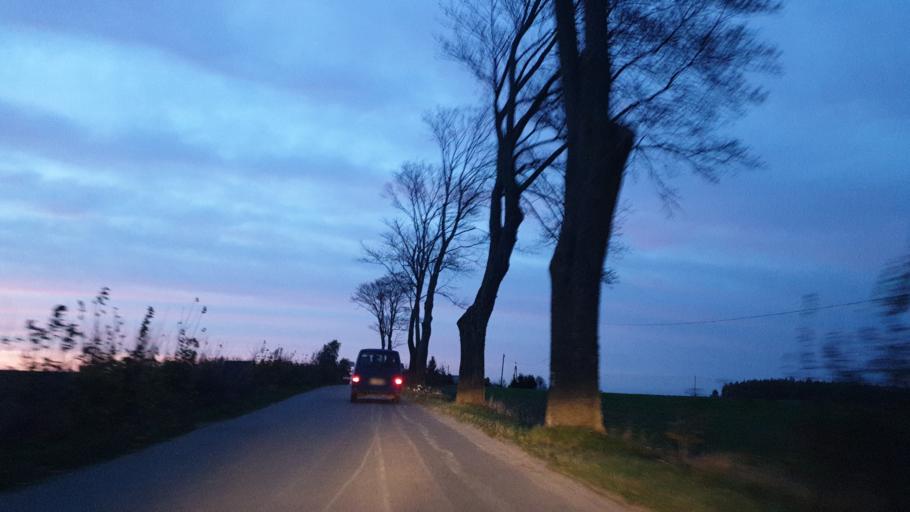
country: PL
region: Pomeranian Voivodeship
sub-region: Powiat pucki
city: Krokowa
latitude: 54.7755
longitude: 18.2096
